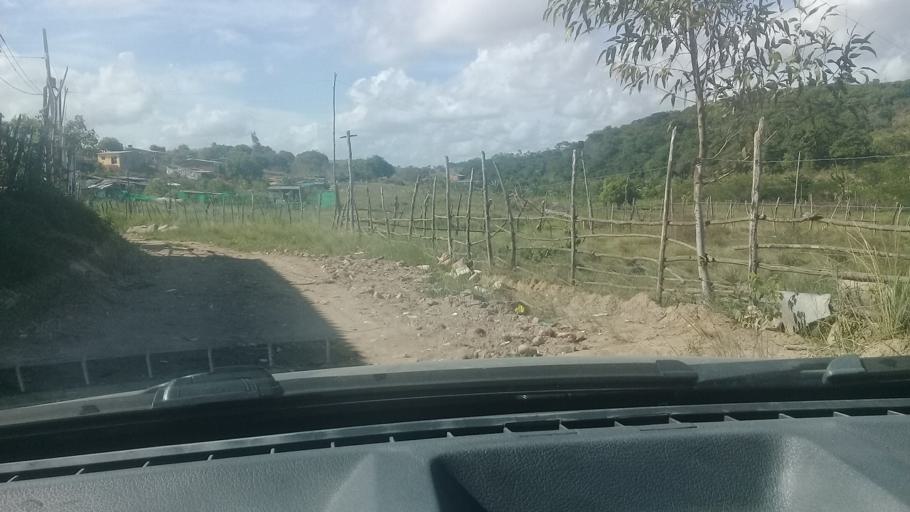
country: BR
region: Pernambuco
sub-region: Jaboatao Dos Guararapes
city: Jaboatao dos Guararapes
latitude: -8.0863
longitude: -35.0338
